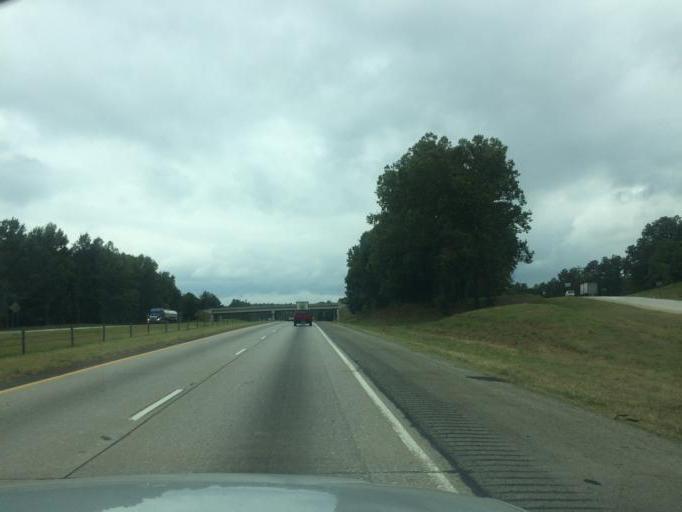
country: US
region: Georgia
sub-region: Banks County
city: Homer
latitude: 34.2996
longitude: -83.4035
